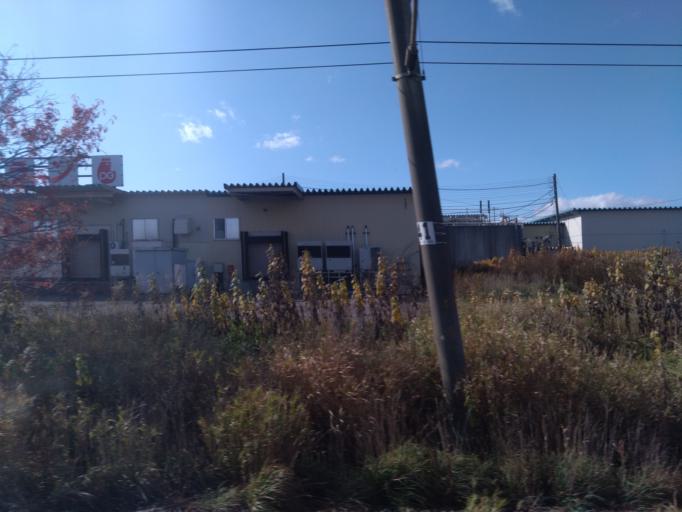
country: JP
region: Hokkaido
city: Kitahiroshima
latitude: 42.9559
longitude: 141.5698
